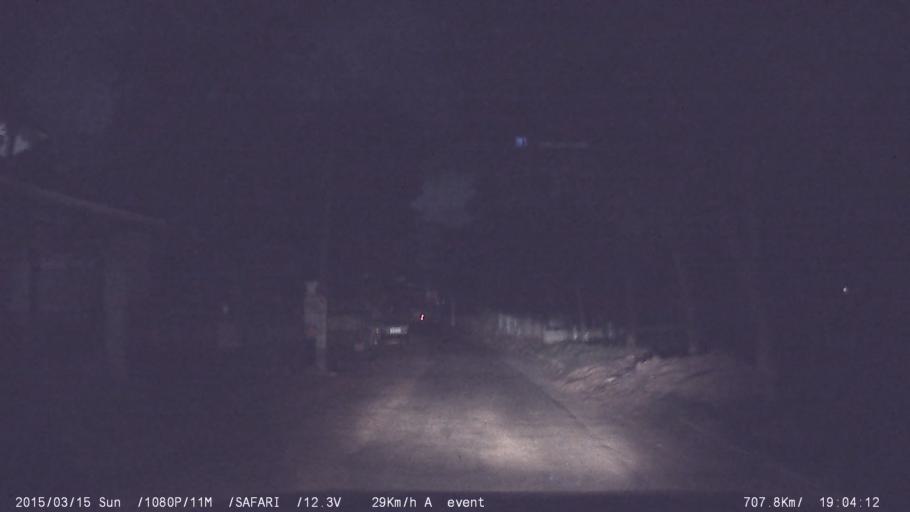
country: IN
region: Kerala
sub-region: Ernakulam
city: Muvattupuzha
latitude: 9.8820
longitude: 76.6434
